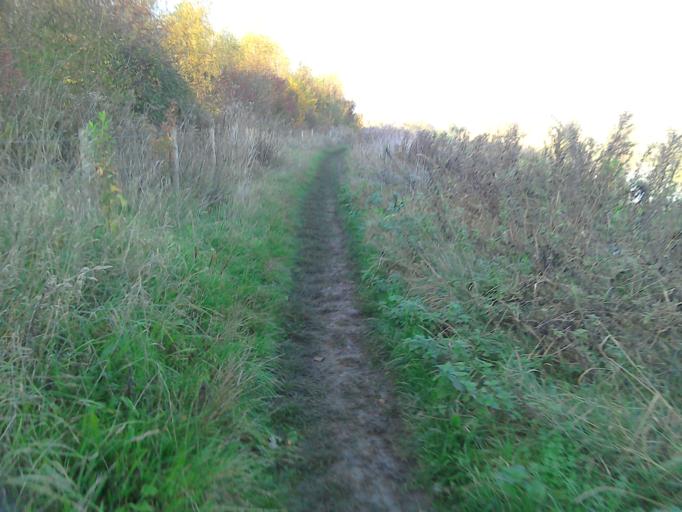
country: GB
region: England
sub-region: Oxfordshire
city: Radley
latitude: 51.7009
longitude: -1.2319
